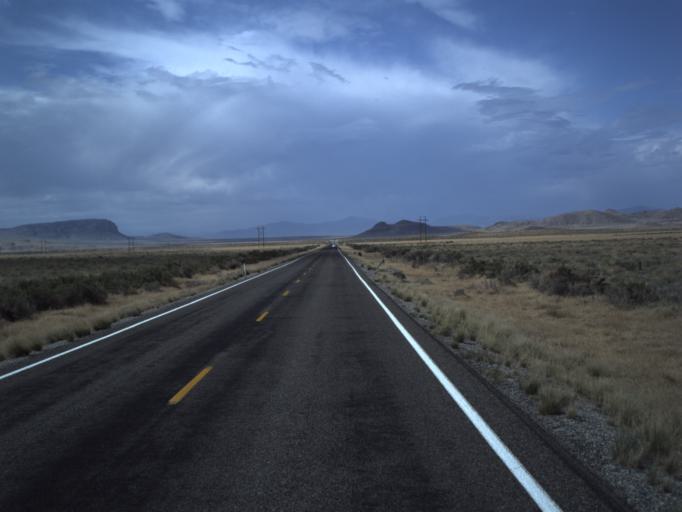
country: US
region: Utah
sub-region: Tooele County
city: Wendover
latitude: 41.4168
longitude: -113.9152
